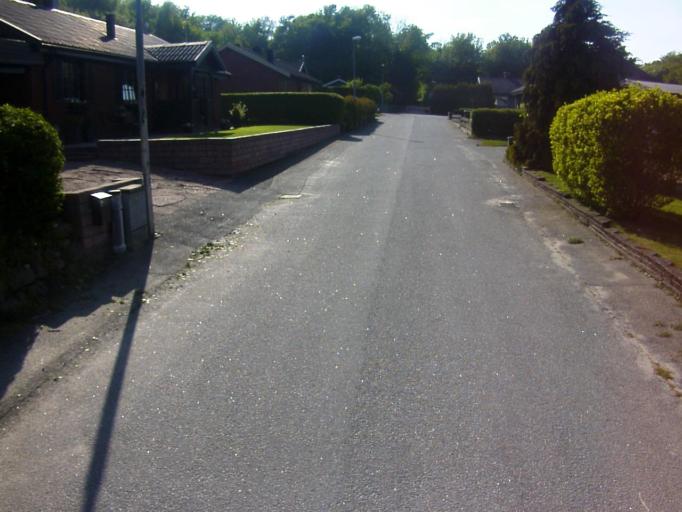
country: SE
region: Blekinge
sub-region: Karlshamns Kommun
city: Morrum
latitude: 56.0383
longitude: 14.7715
